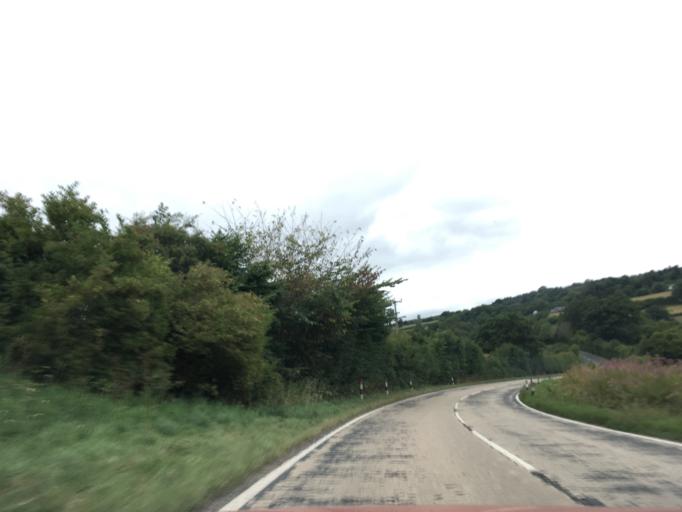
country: GB
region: Wales
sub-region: Blaenau Gwent
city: Brynmawr
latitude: 51.8840
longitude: -3.2270
